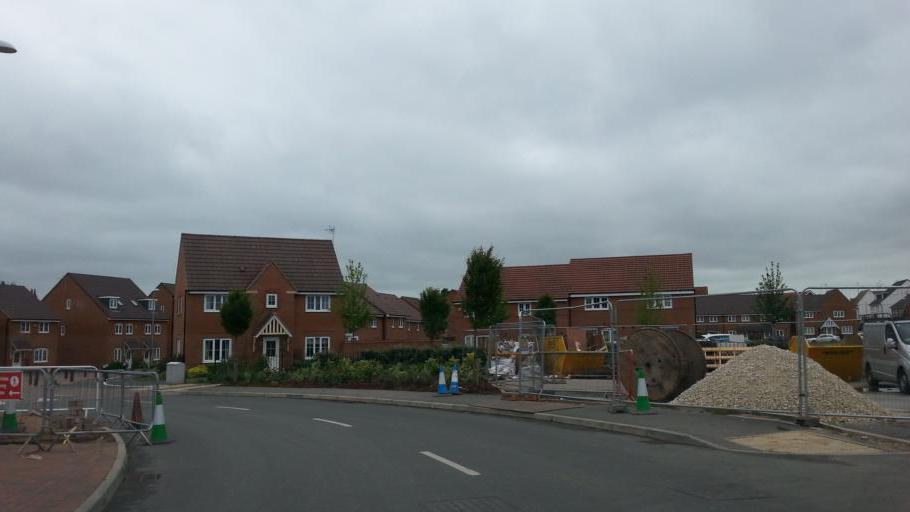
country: GB
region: England
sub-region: Nottinghamshire
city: Hucknall
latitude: 53.0402
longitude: -1.1930
